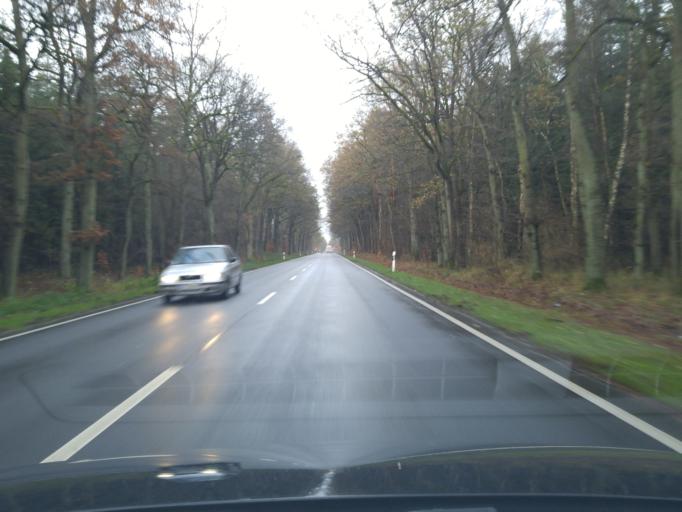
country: DE
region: Lower Saxony
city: Dedelstorf
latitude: 52.7003
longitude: 10.4764
